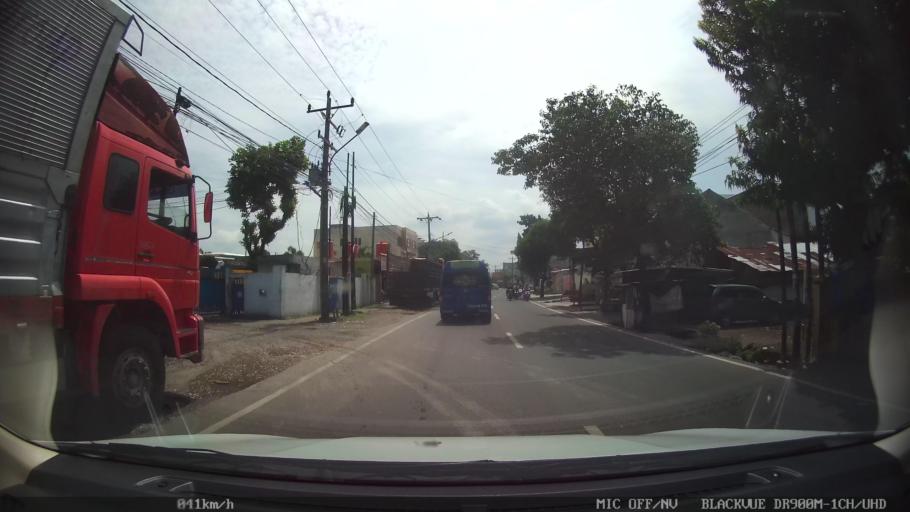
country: ID
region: North Sumatra
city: Sunggal
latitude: 3.5786
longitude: 98.6277
